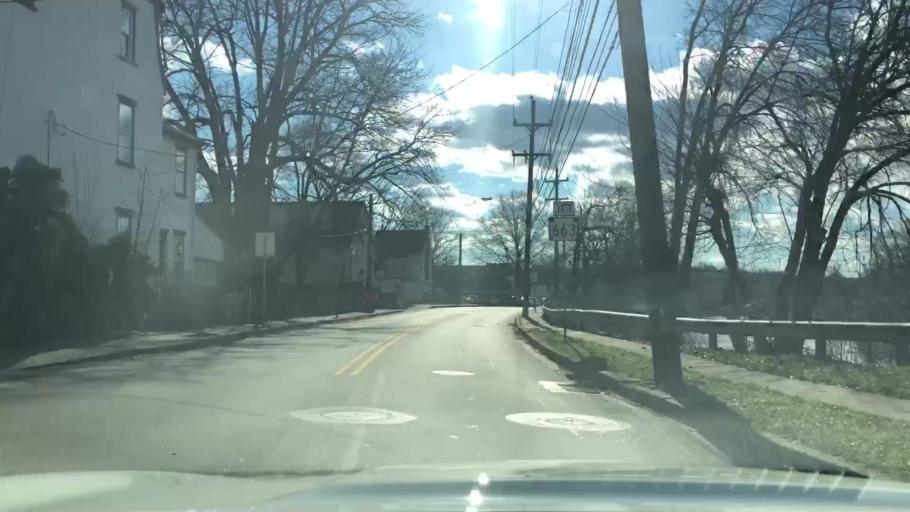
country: US
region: Pennsylvania
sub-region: Montgomery County
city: Pottstown
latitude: 40.2493
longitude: -75.6546
